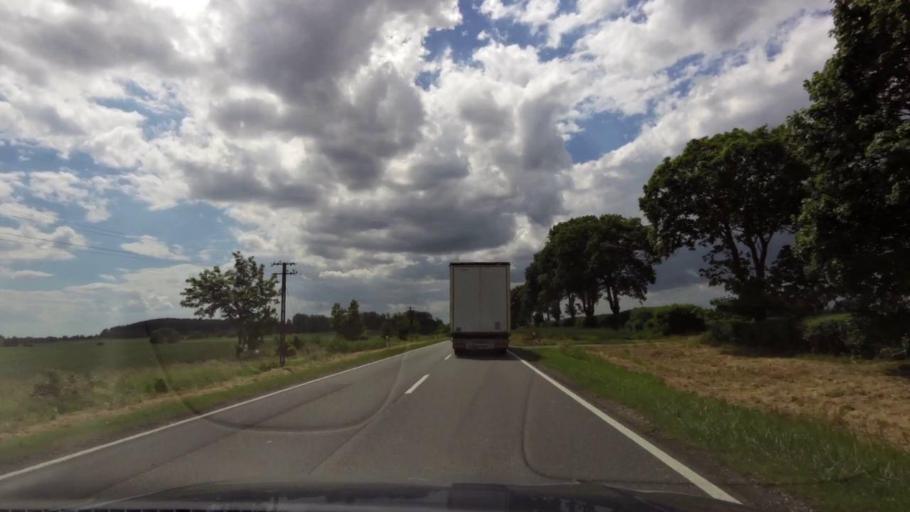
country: PL
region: West Pomeranian Voivodeship
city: Trzcinsko Zdroj
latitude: 52.9695
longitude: 14.6338
